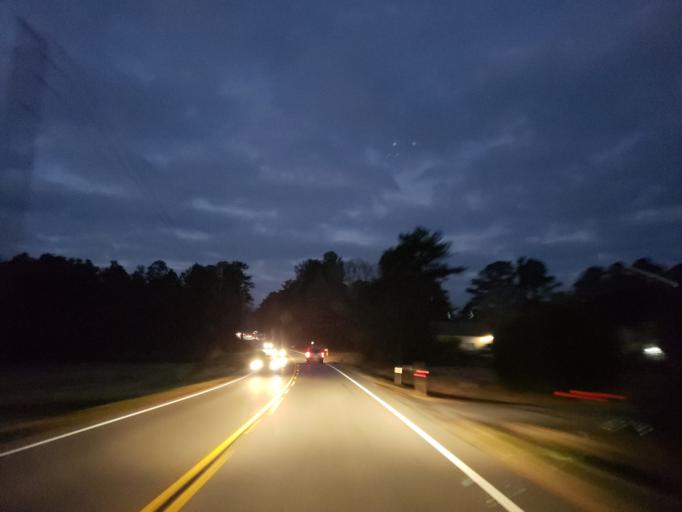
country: US
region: Georgia
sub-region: Polk County
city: Rockmart
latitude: 33.9036
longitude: -84.9955
